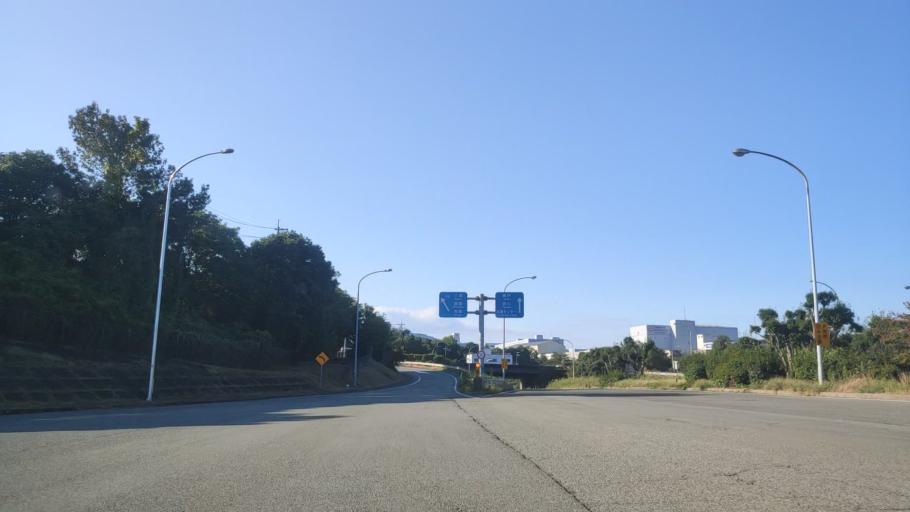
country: JP
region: Hyogo
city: Sandacho
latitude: 34.8356
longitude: 135.2352
